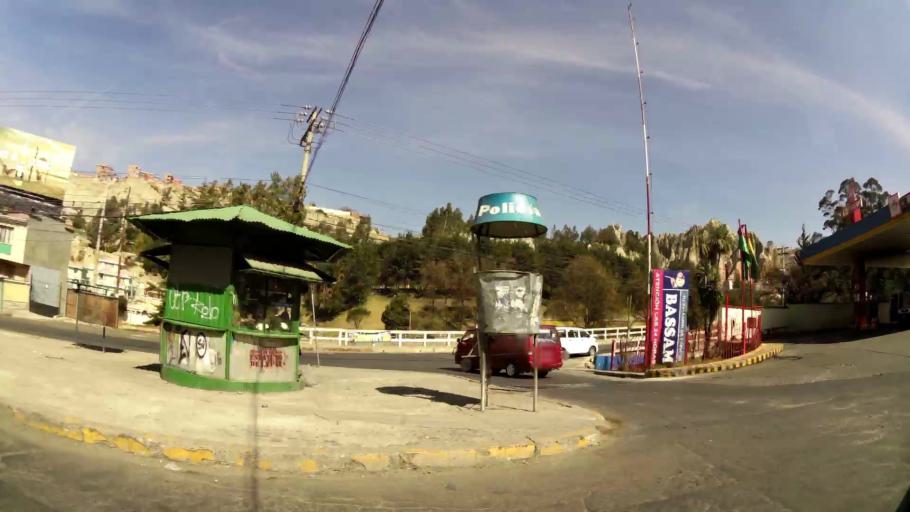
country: BO
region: La Paz
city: La Paz
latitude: -16.5222
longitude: -68.1149
